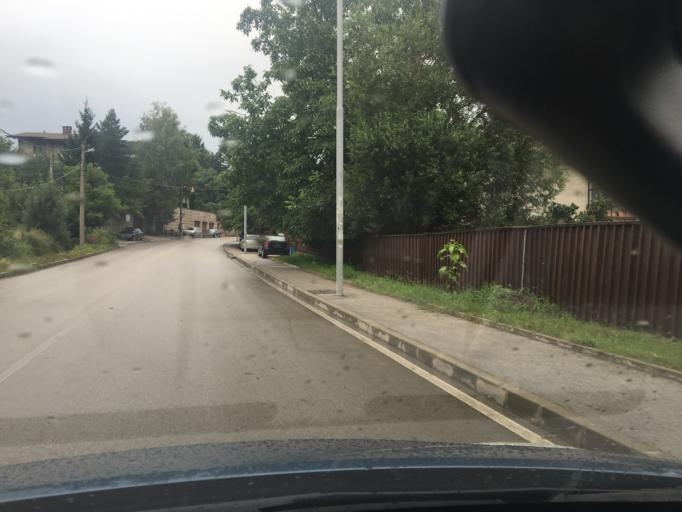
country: BG
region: Sofia-Capital
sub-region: Stolichna Obshtina
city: Sofia
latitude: 42.6323
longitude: 23.3054
